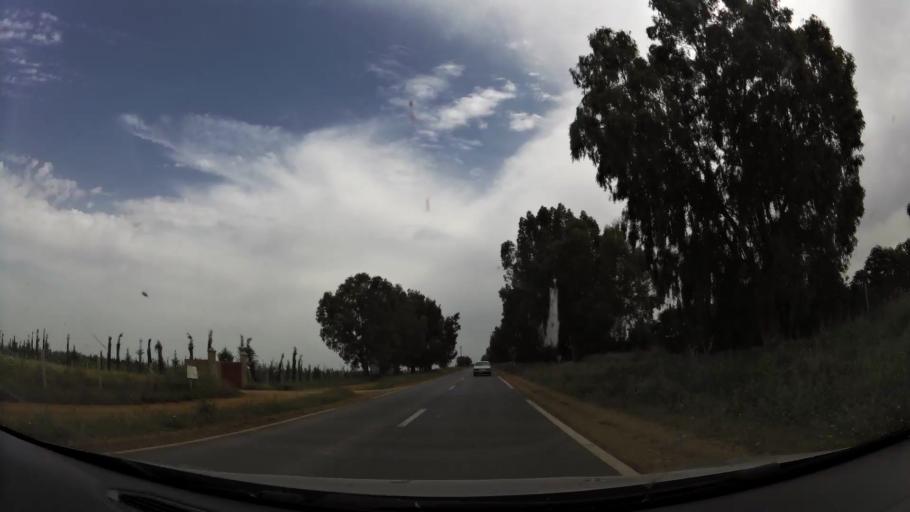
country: MA
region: Rabat-Sale-Zemmour-Zaer
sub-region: Khemisset
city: Tiflet
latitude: 33.8205
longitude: -6.2724
